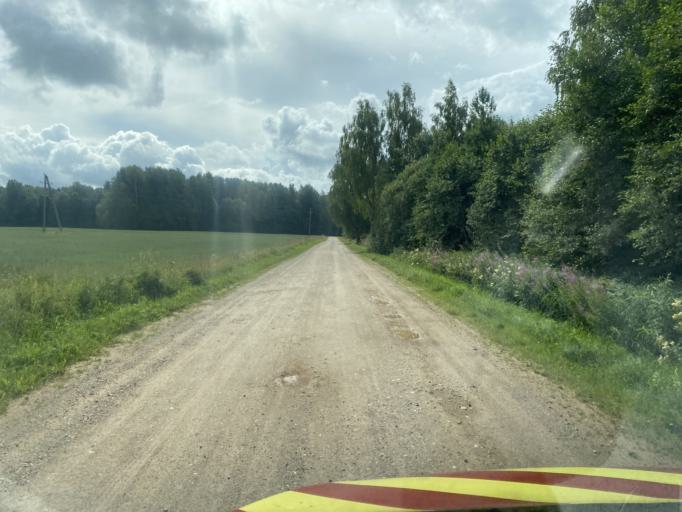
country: EE
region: Viljandimaa
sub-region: Karksi vald
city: Karksi-Nuia
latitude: 58.0807
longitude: 25.5163
